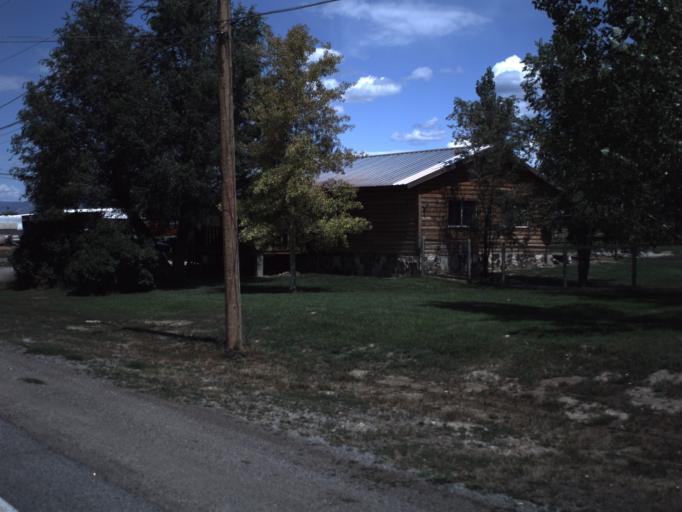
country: US
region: Utah
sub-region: Sanpete County
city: Mount Pleasant
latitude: 39.4858
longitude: -111.4961
